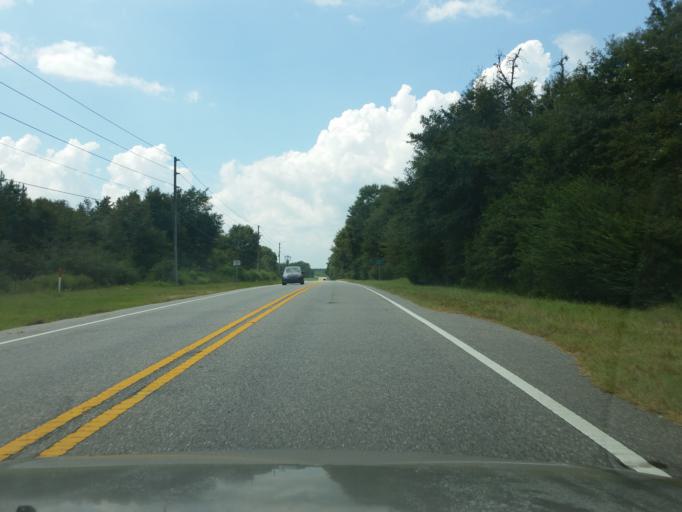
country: US
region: Alabama
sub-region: Baldwin County
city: Elberta
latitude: 30.5350
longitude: -87.5288
